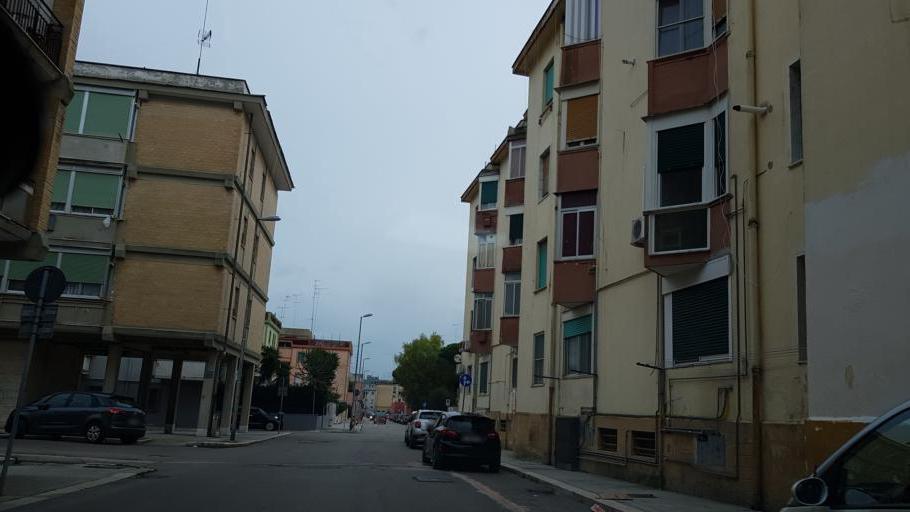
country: IT
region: Apulia
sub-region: Provincia di Brindisi
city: Brindisi
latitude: 40.6283
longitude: 17.9284
